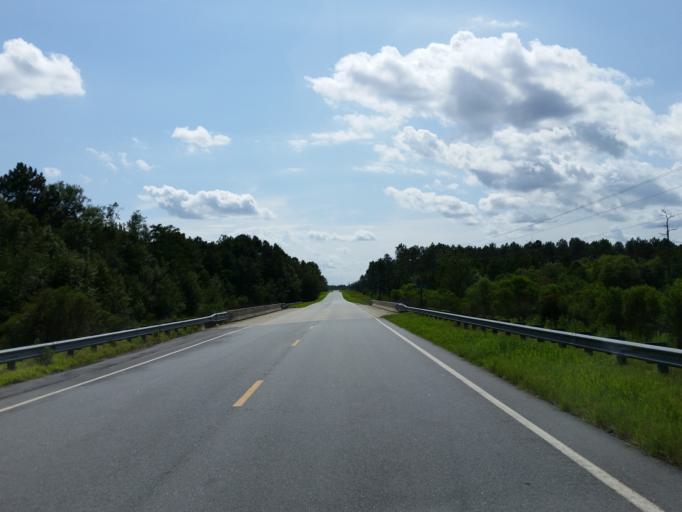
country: US
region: Georgia
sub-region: Turner County
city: Ashburn
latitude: 31.6354
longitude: -83.4952
